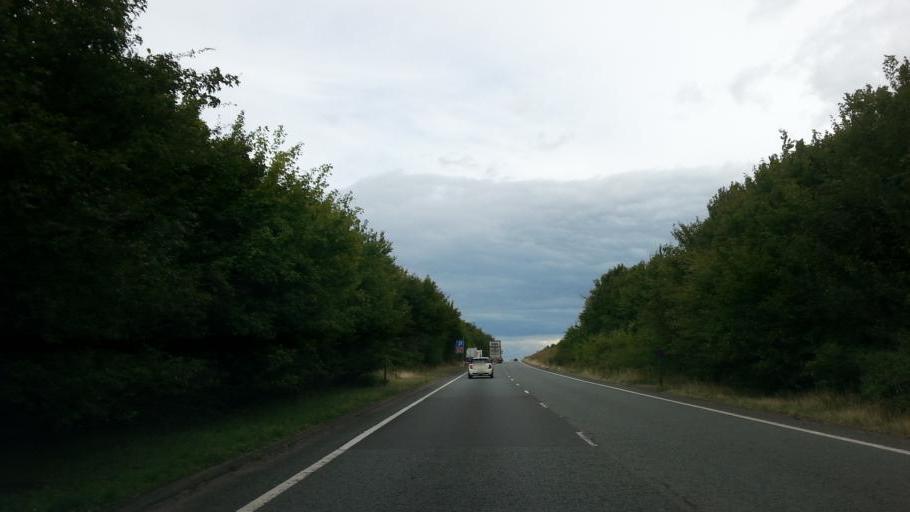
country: GB
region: England
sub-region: Cambridgeshire
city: Duxford
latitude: 52.0924
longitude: 0.2029
